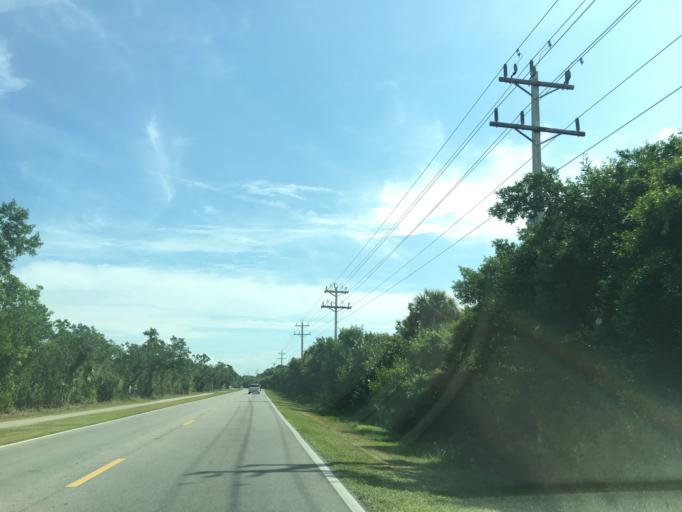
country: US
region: Florida
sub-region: Lee County
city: Saint James City
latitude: 26.4411
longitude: -82.1033
